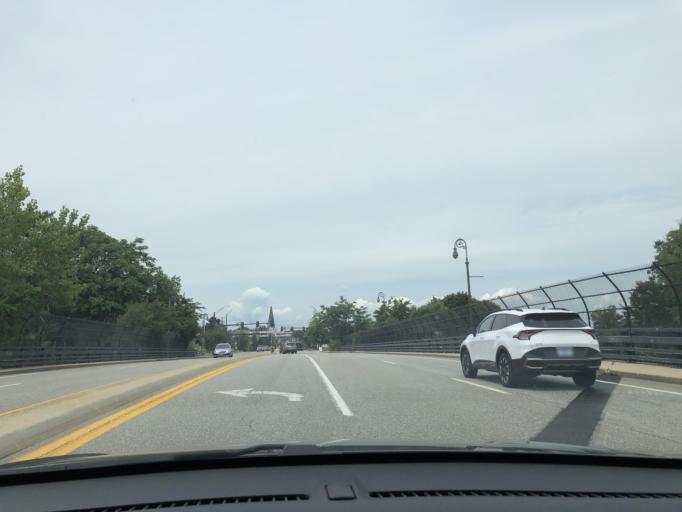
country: US
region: New Hampshire
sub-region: Merrimack County
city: Concord
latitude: 43.1961
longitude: -71.5292
